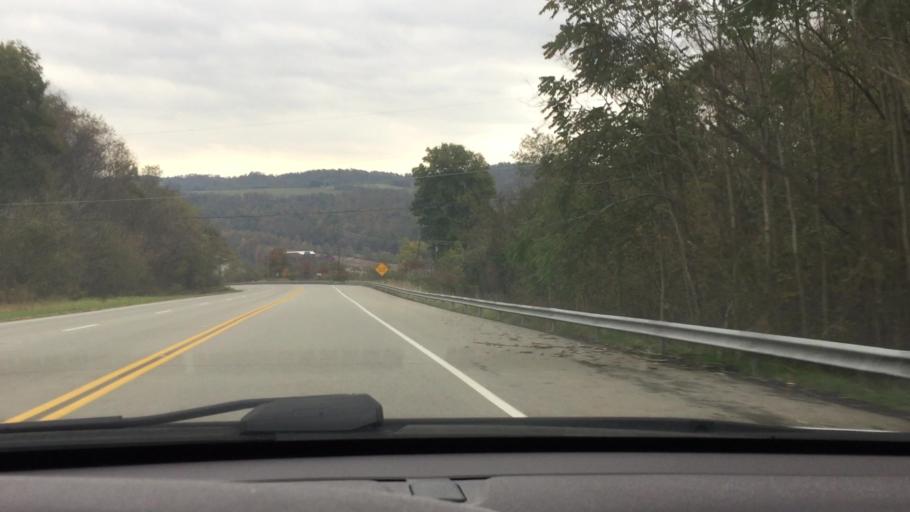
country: US
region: Pennsylvania
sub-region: Washington County
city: California
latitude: 40.0839
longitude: -79.8910
